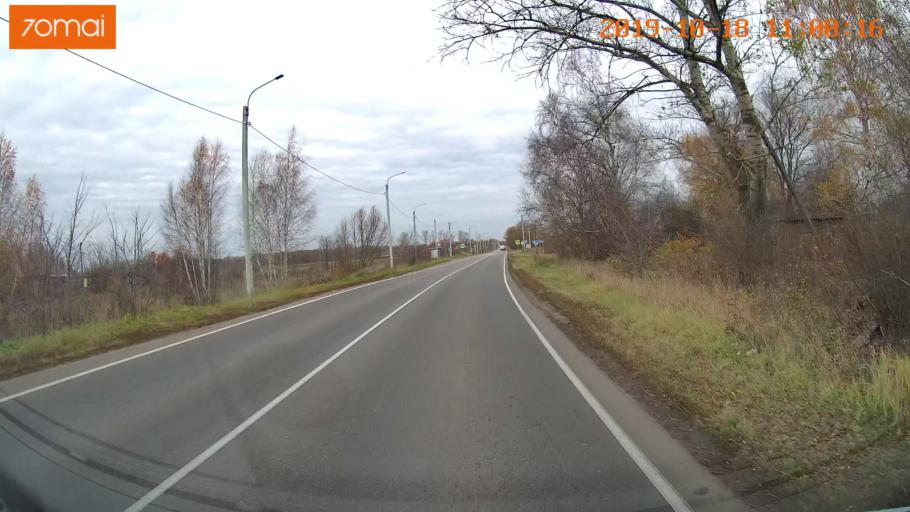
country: RU
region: Tula
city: Yepifan'
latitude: 53.8412
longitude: 38.5527
